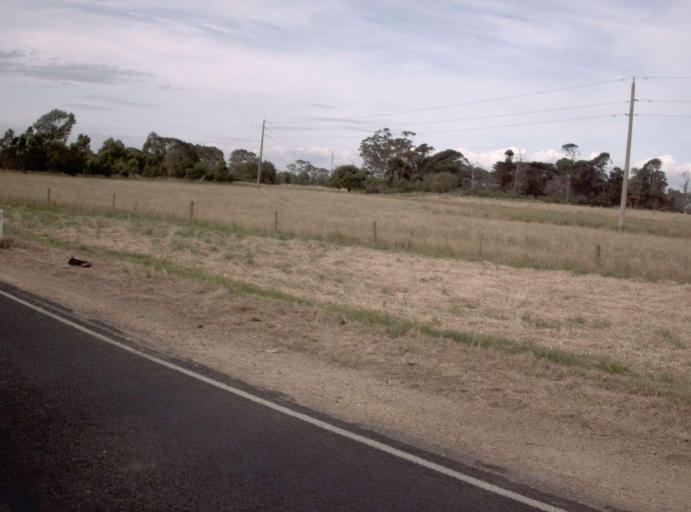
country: AU
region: Victoria
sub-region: Wellington
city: Heyfield
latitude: -38.0037
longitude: 146.7807
